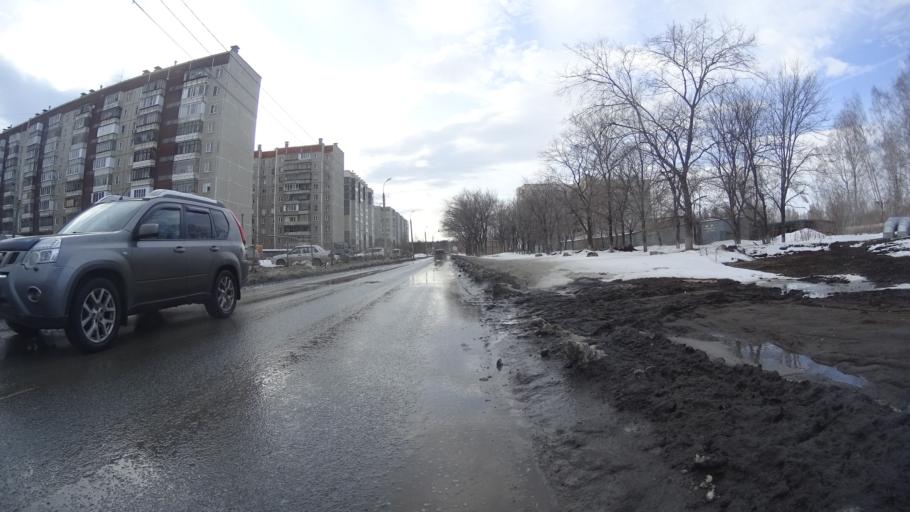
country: RU
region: Chelyabinsk
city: Roshchino
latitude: 55.1988
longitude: 61.3095
